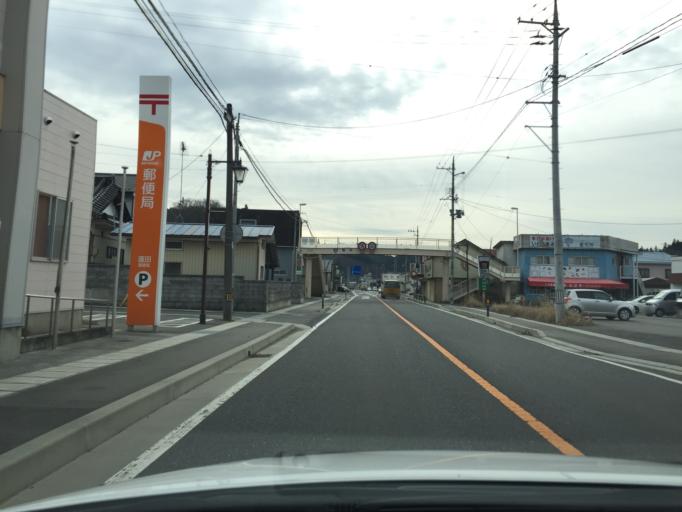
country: JP
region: Fukushima
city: Ishikawa
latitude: 37.2425
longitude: 140.5692
